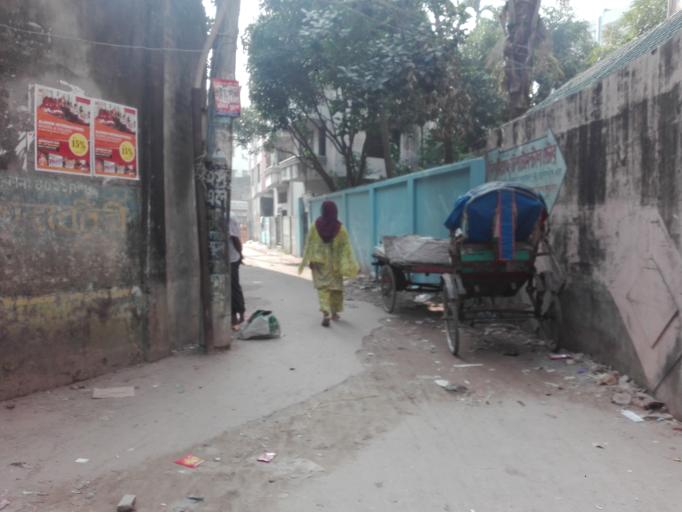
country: BD
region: Dhaka
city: Azimpur
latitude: 23.7939
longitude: 90.3606
